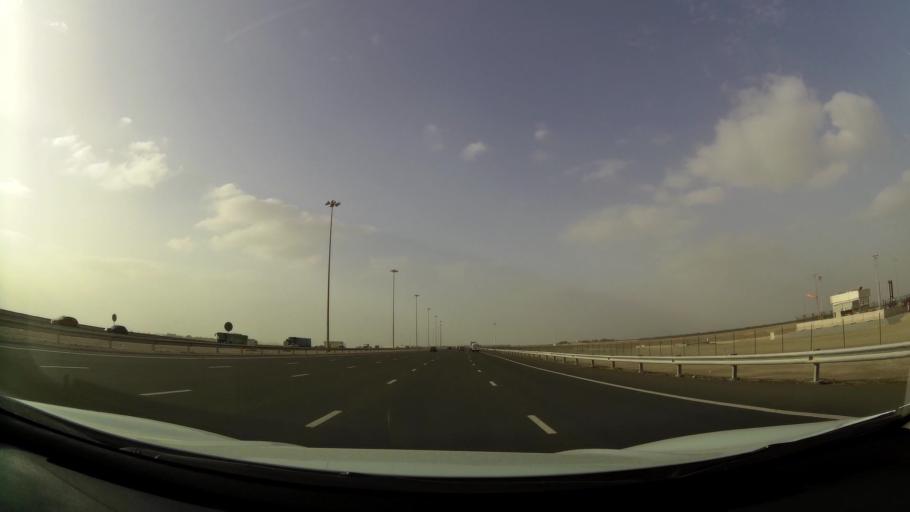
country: AE
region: Abu Dhabi
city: Abu Dhabi
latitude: 24.5356
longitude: 54.4864
